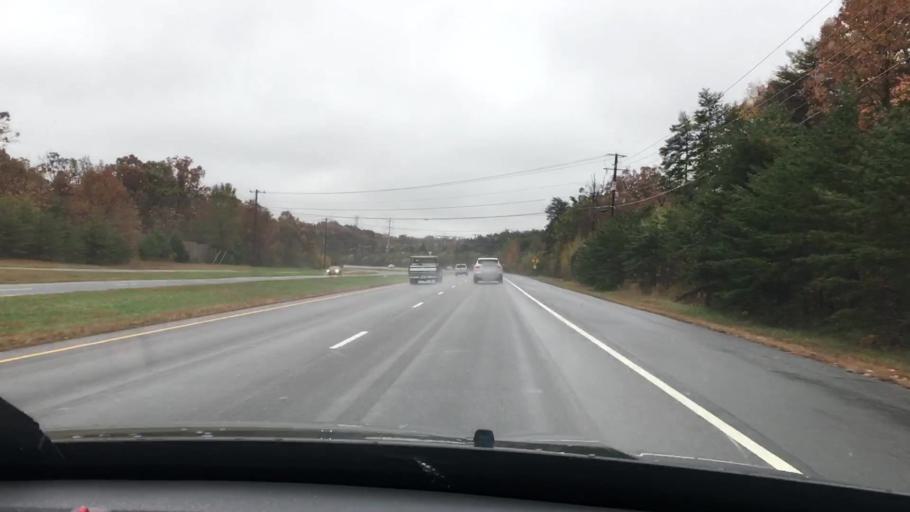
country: US
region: Virginia
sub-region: Prince William County
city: Lake Ridge
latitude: 38.7237
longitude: -77.2808
